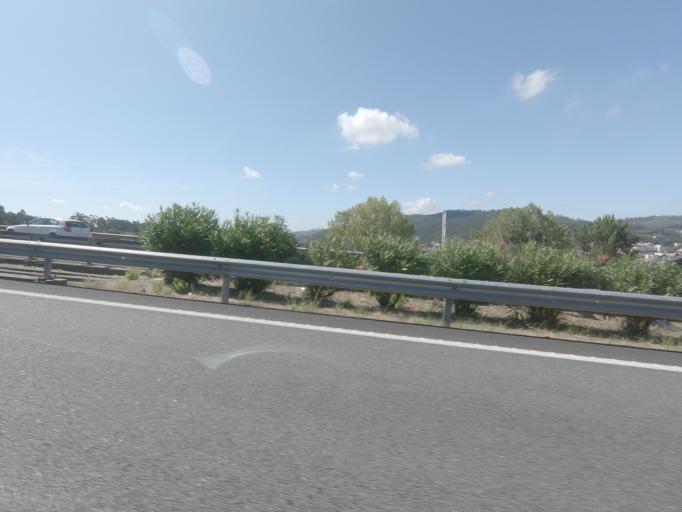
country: PT
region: Porto
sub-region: Valongo
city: Valongo
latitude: 41.1967
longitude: -8.4892
